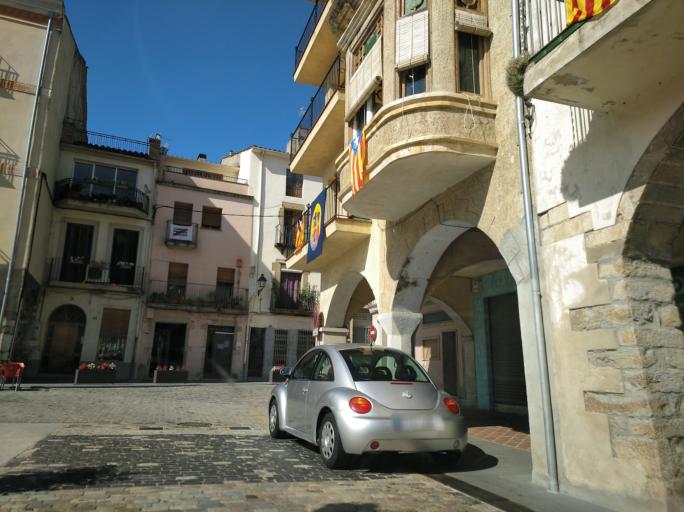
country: ES
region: Catalonia
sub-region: Provincia de Girona
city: la Cellera de Ter
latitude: 42.0092
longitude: 2.6029
